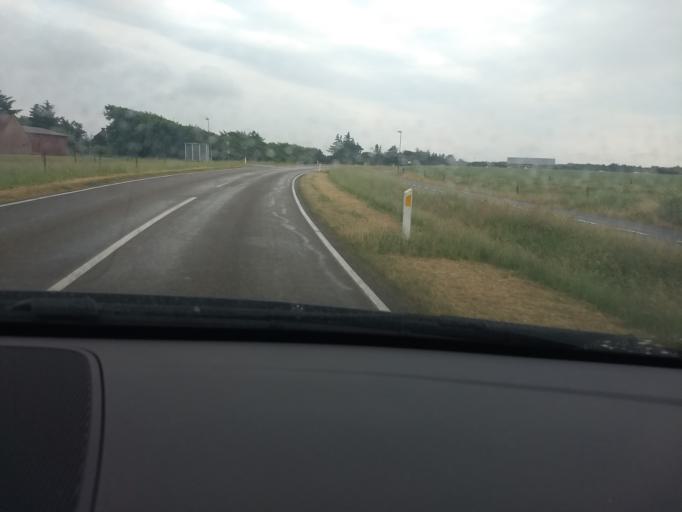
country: DK
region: South Denmark
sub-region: Fano Kommune
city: Nordby
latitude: 55.4242
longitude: 8.3992
